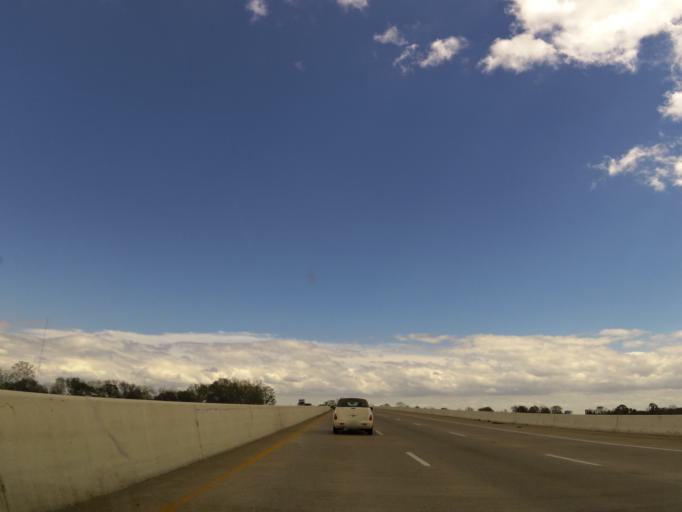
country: US
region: Tennessee
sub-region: Shelby County
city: Memphis
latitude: 35.1537
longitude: -90.1058
